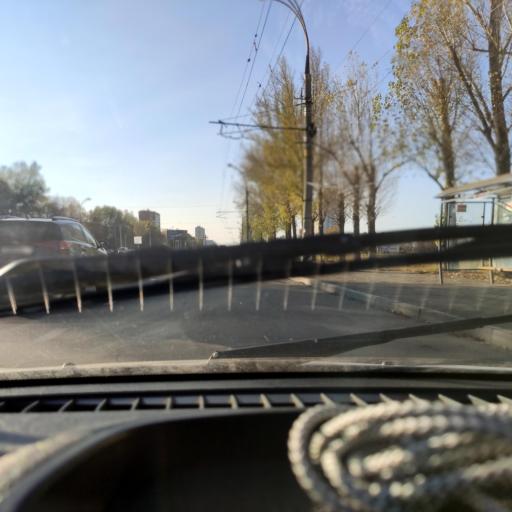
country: RU
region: Samara
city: Tol'yatti
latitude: 53.5187
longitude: 49.2583
